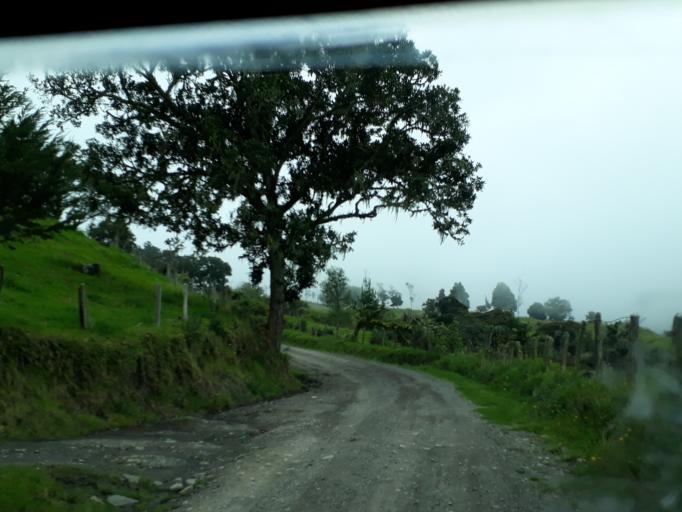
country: CO
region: Cundinamarca
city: Carmen de Carupa
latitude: 5.3727
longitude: -73.9730
